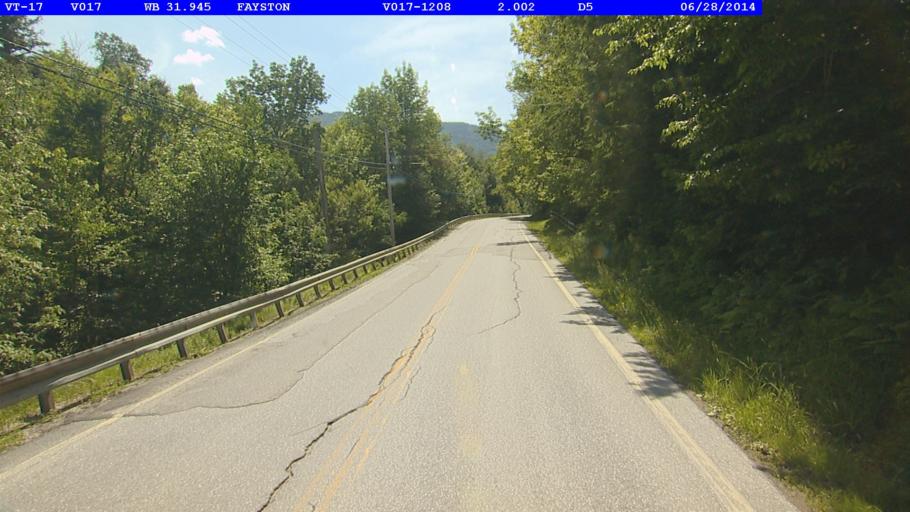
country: US
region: Vermont
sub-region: Addison County
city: Bristol
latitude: 44.2044
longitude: -72.9035
